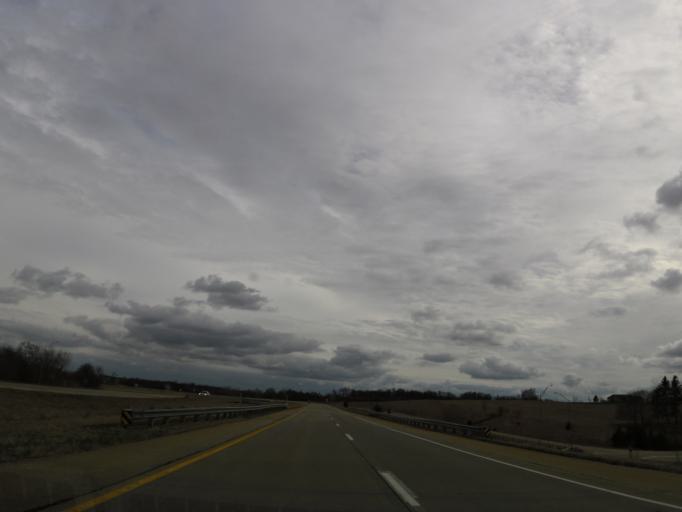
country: US
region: Iowa
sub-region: Bremer County
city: Denver
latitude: 42.6724
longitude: -92.3447
